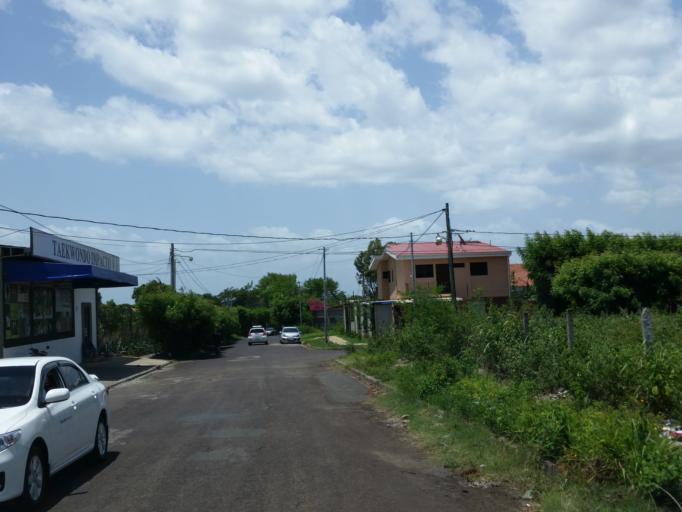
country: NI
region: Managua
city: Managua
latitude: 12.1162
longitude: -86.2707
